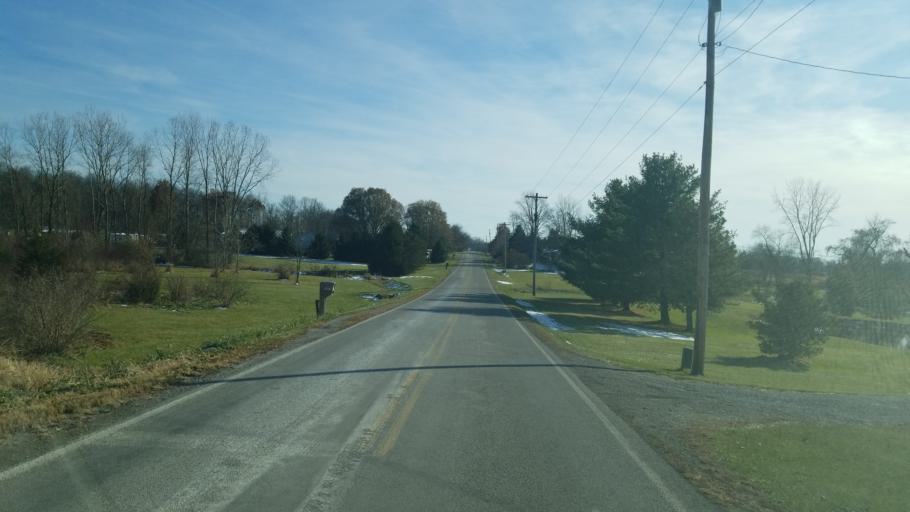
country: US
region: Ohio
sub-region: Lorain County
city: Camden
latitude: 41.1850
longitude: -82.3540
